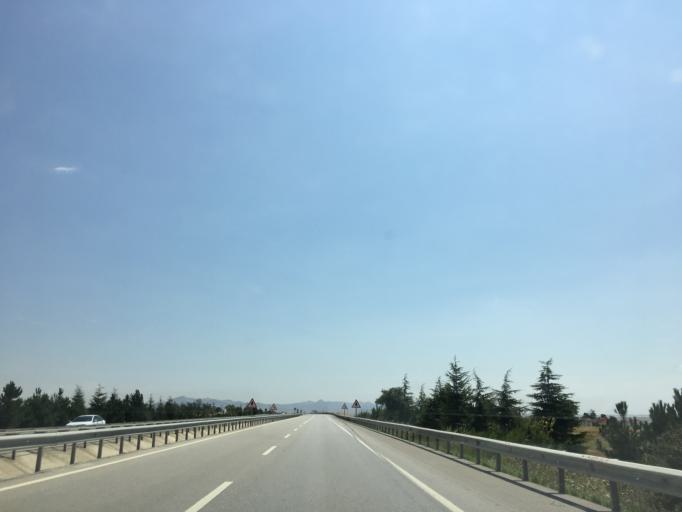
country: TR
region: Eskisehir
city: Sivrihisar
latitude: 39.4587
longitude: 31.3878
